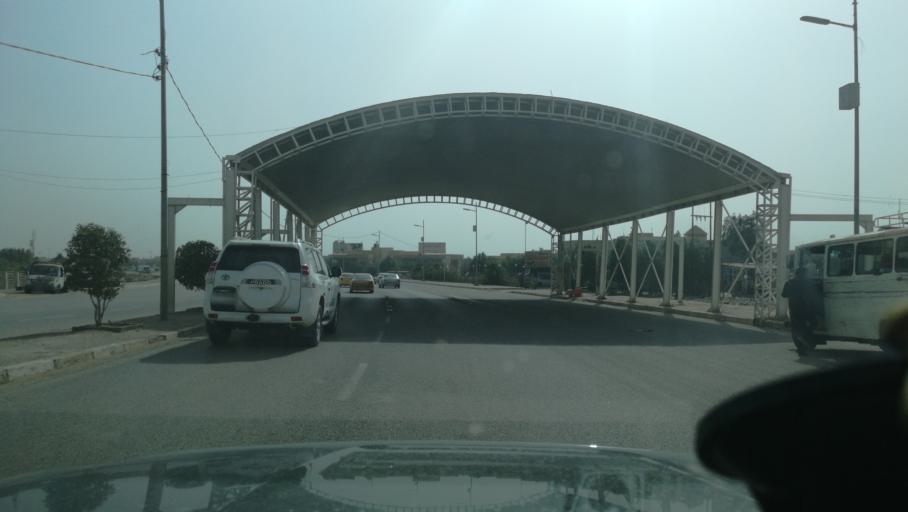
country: IQ
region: Dhi Qar
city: An Nasiriyah
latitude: 31.0888
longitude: 46.2436
